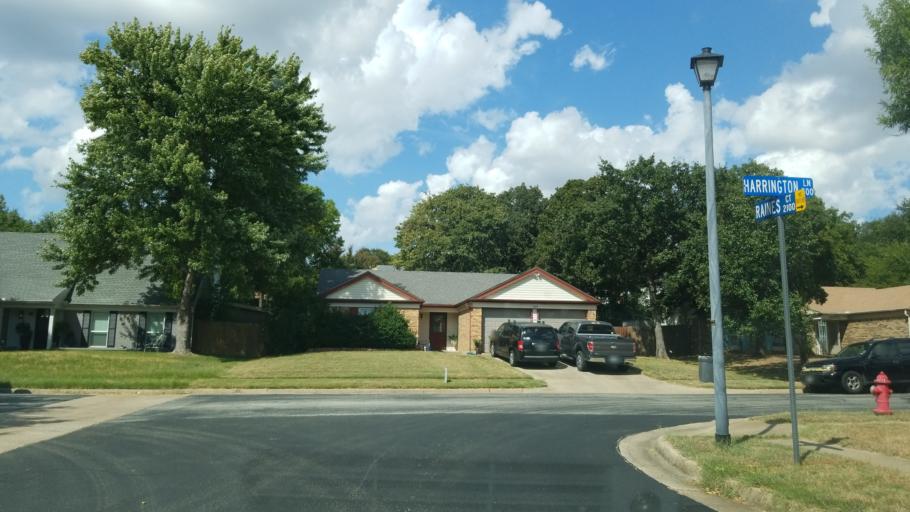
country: US
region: Texas
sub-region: Tarrant County
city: Euless
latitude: 32.8670
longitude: -97.0754
